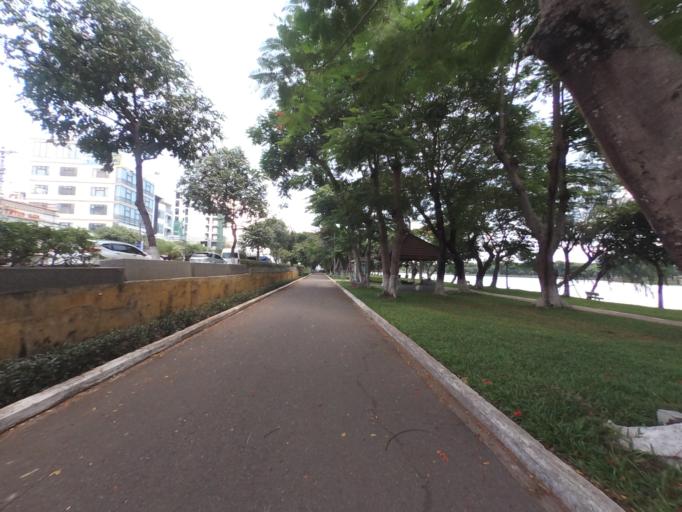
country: VN
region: Da Nang
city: Da Nang
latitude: 16.0605
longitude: 108.2055
